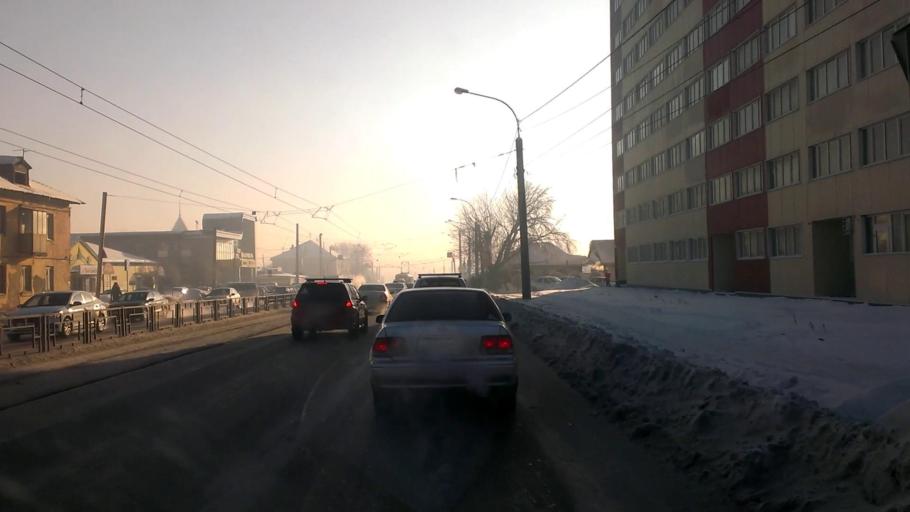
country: RU
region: Altai Krai
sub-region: Gorod Barnaulskiy
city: Barnaul
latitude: 53.3455
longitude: 83.7328
